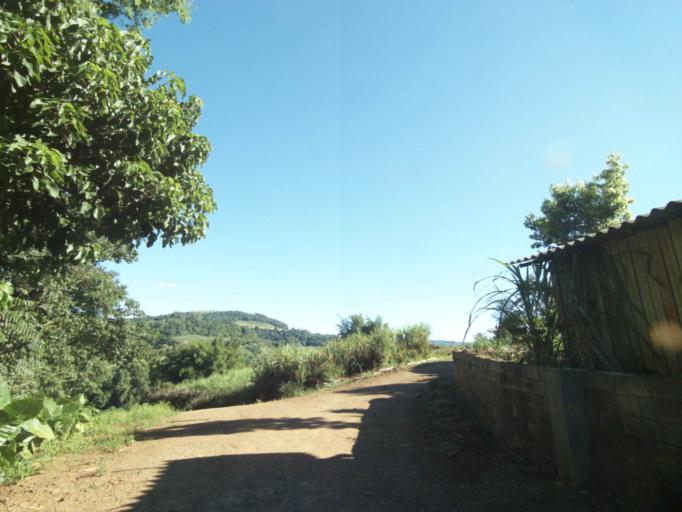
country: BR
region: Parana
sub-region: Ampere
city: Ampere
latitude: -26.1746
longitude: -53.3659
